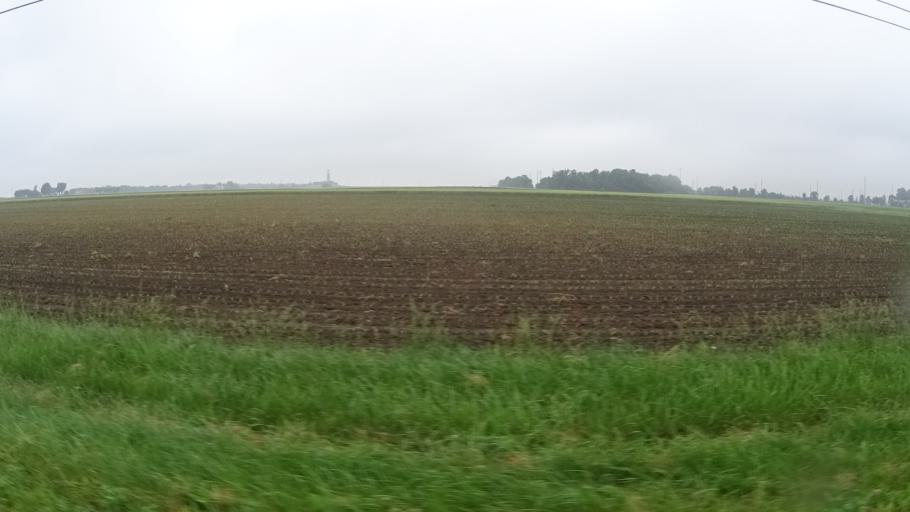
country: US
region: Ohio
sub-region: Huron County
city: Bellevue
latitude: 41.3264
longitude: -82.8371
